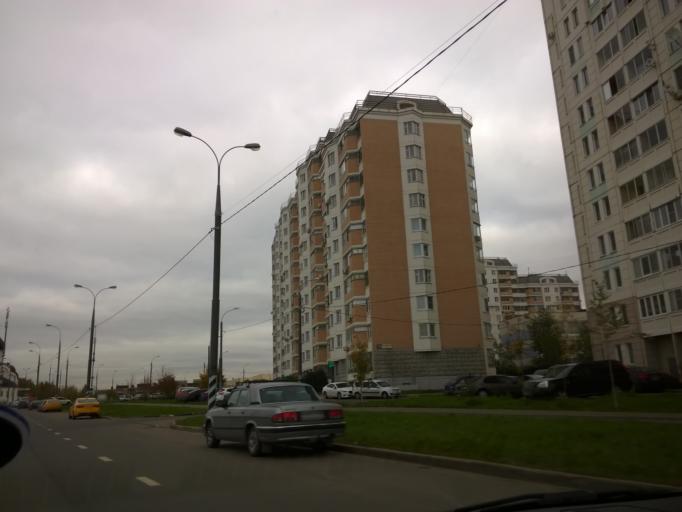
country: RU
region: Moskovskaya
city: Kommunarka
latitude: 55.5307
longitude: 37.5018
